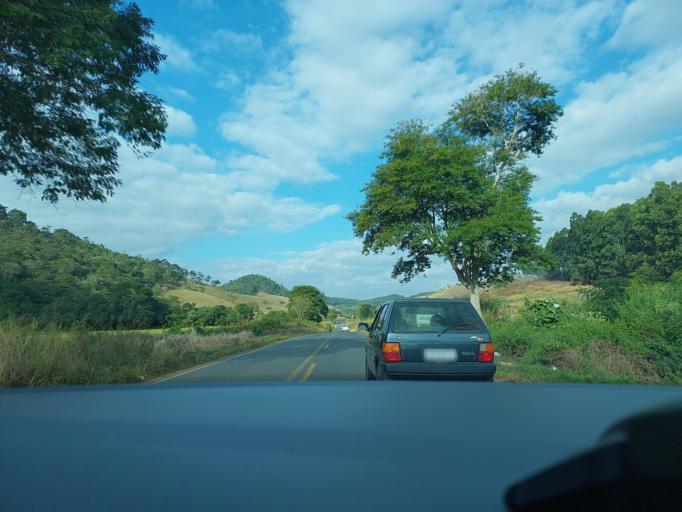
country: BR
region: Minas Gerais
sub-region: Vicosa
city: Vicosa
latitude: -20.8294
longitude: -42.7632
